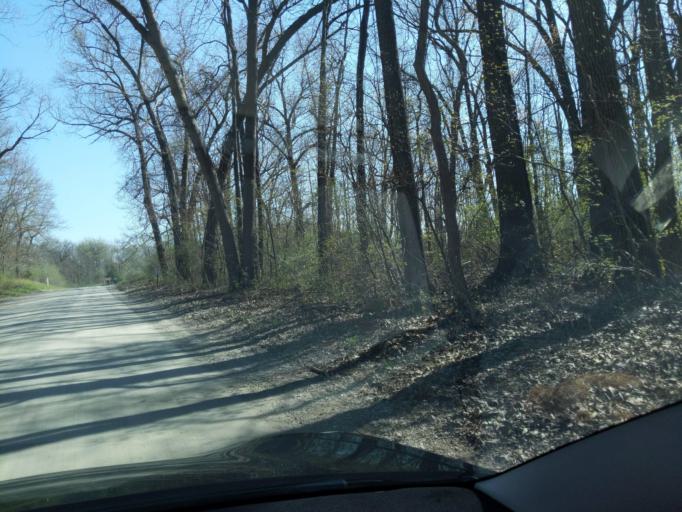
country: US
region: Michigan
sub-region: Washtenaw County
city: Chelsea
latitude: 42.3845
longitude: -84.0836
